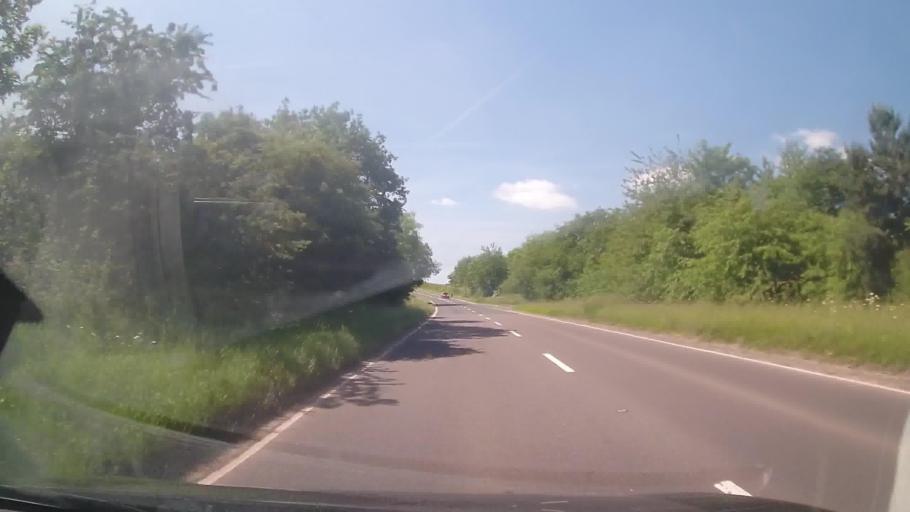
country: GB
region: England
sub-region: Herefordshire
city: Kimbolton
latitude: 52.2871
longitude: -2.7071
